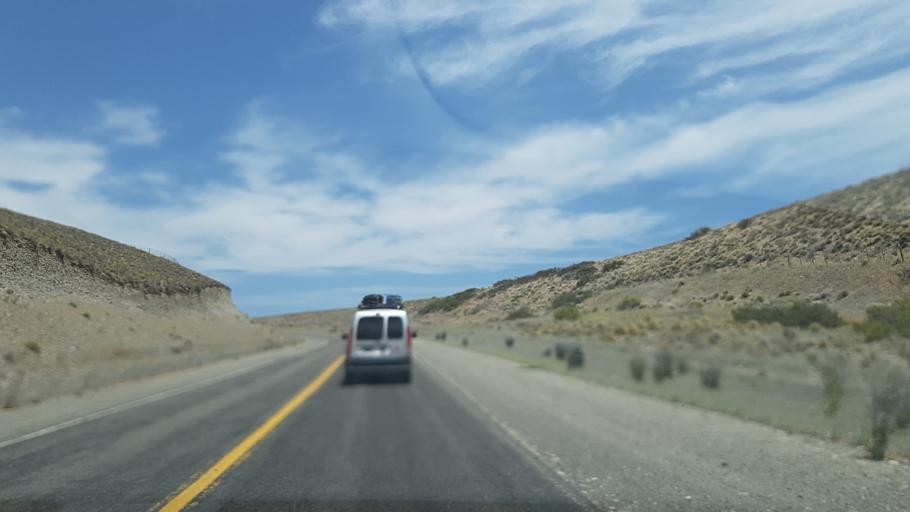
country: AR
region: Rio Negro
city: Pilcaniyeu
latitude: -40.4859
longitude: -70.6799
